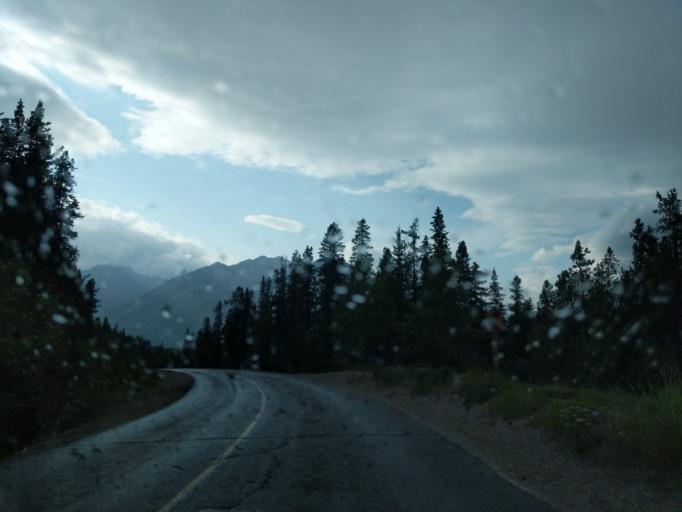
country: CA
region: Alberta
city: Banff
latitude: 51.1597
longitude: -115.5664
